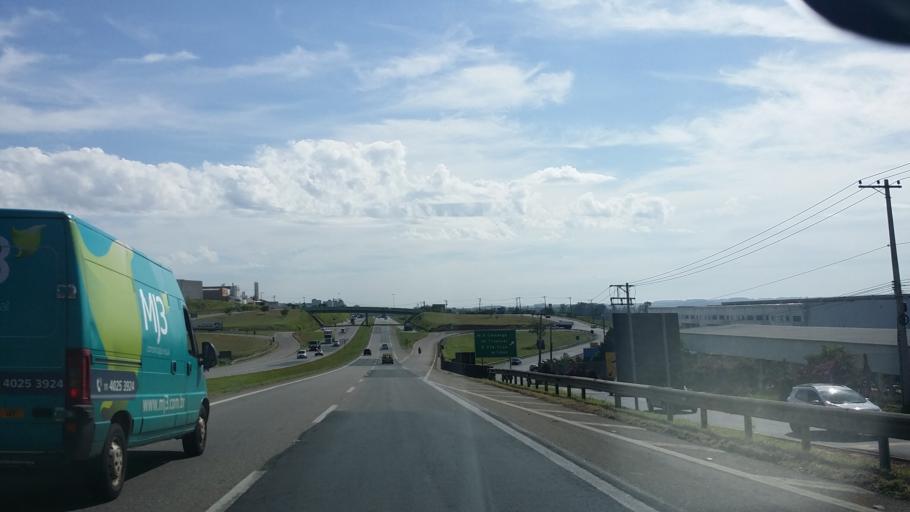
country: BR
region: Sao Paulo
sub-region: Indaiatuba
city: Indaiatuba
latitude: -23.1149
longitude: -47.2142
